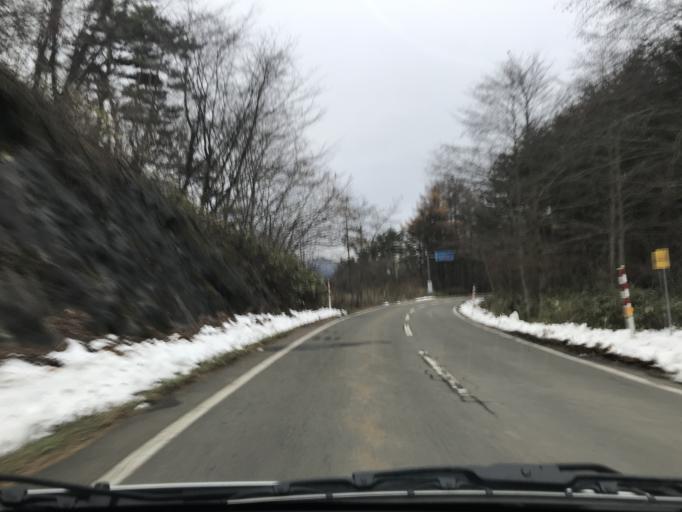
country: JP
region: Iwate
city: Mizusawa
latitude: 39.1499
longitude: 141.3628
